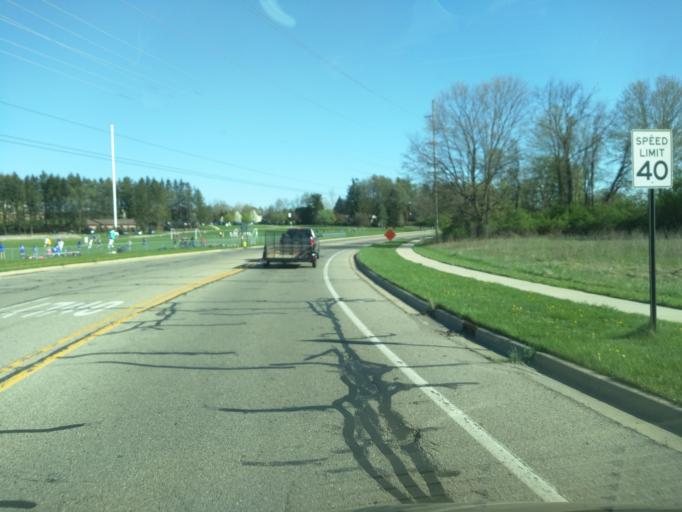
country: US
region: Michigan
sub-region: Eaton County
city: Waverly
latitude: 42.7547
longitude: -84.6426
